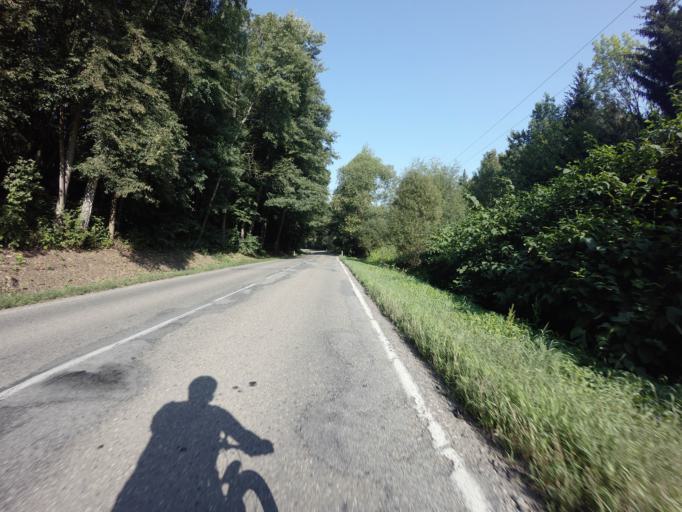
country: CZ
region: Central Bohemia
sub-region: Okres Benesov
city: Benesov
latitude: 49.7929
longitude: 14.6669
